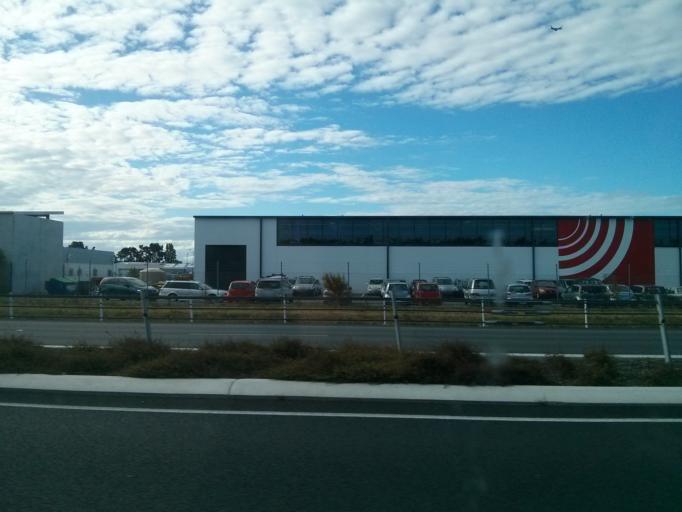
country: NZ
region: Canterbury
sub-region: Christchurch City
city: Christchurch
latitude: -43.4732
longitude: 172.5635
